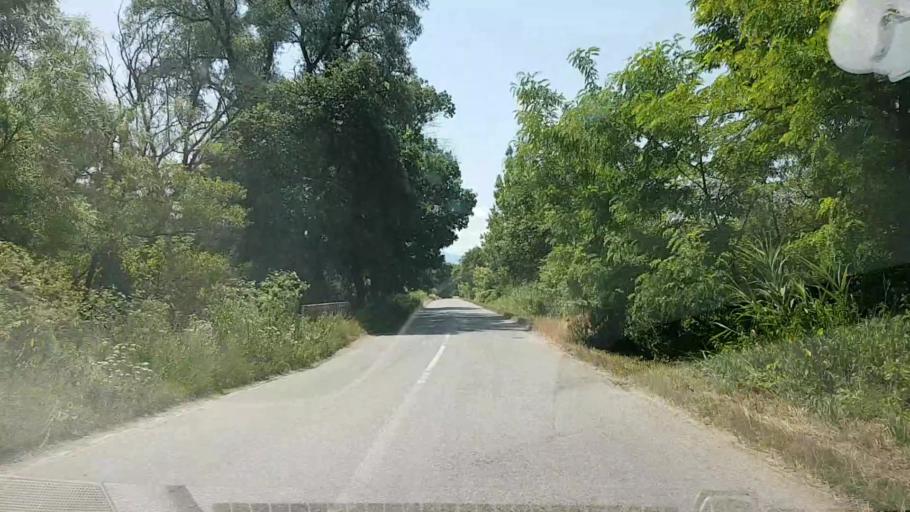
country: RO
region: Brasov
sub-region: Comuna Voila
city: Voila
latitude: 45.8490
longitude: 24.8325
